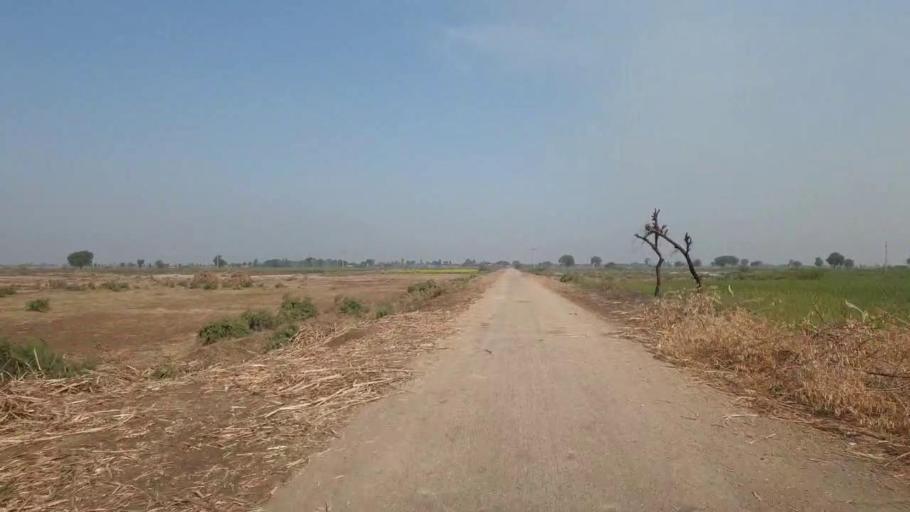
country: PK
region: Sindh
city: Mirwah Gorchani
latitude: 25.3691
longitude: 69.1613
